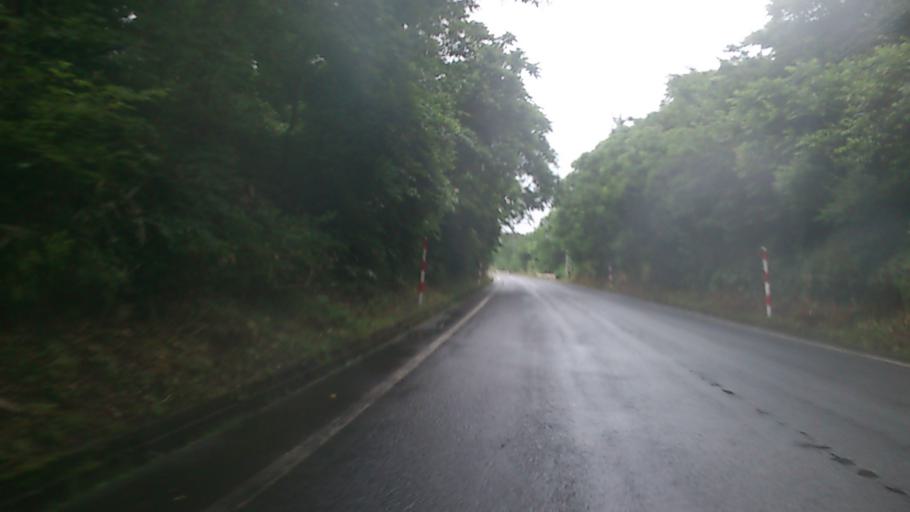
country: JP
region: Akita
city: Noshiromachi
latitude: 40.4232
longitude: 139.9476
